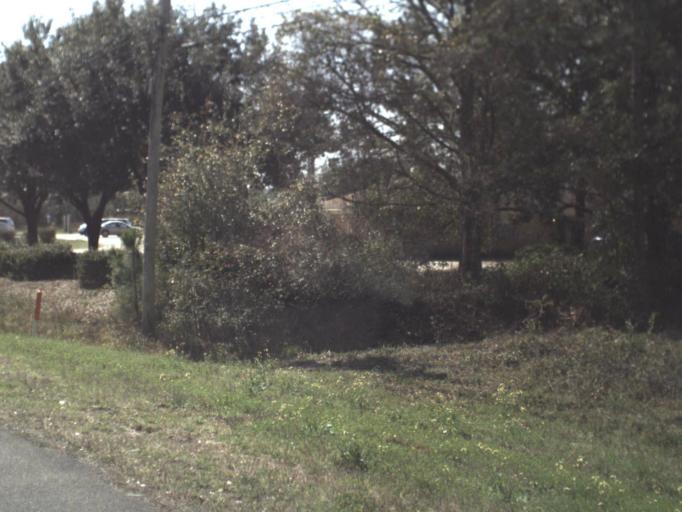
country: US
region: Florida
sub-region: Bay County
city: Lynn Haven
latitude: 30.2240
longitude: -85.6626
